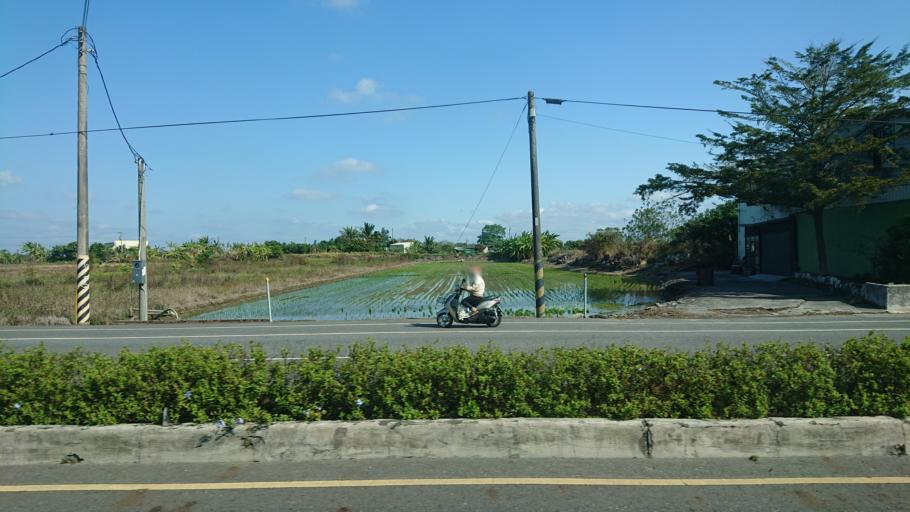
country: TW
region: Taiwan
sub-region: Chiayi
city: Taibao
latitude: 23.4401
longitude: 120.3818
